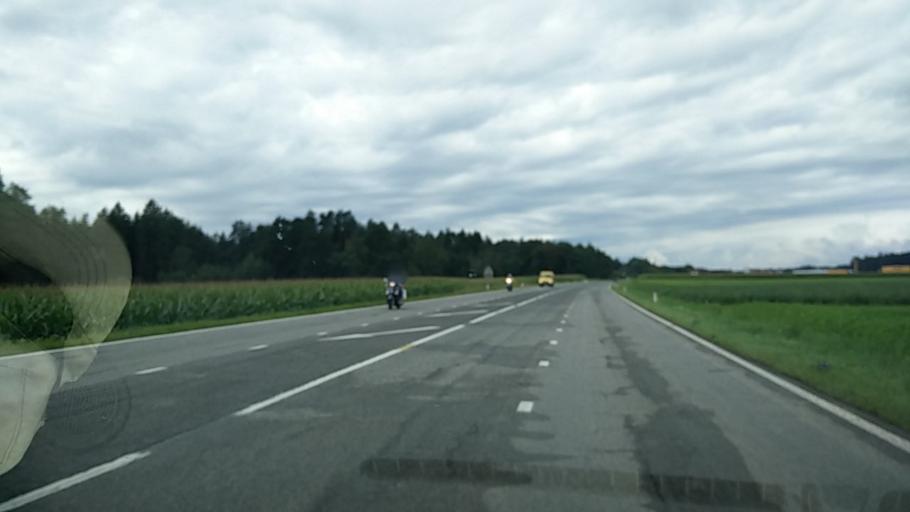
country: AT
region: Carinthia
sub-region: Politischer Bezirk Klagenfurt Land
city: Poggersdorf
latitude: 46.6422
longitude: 14.4628
